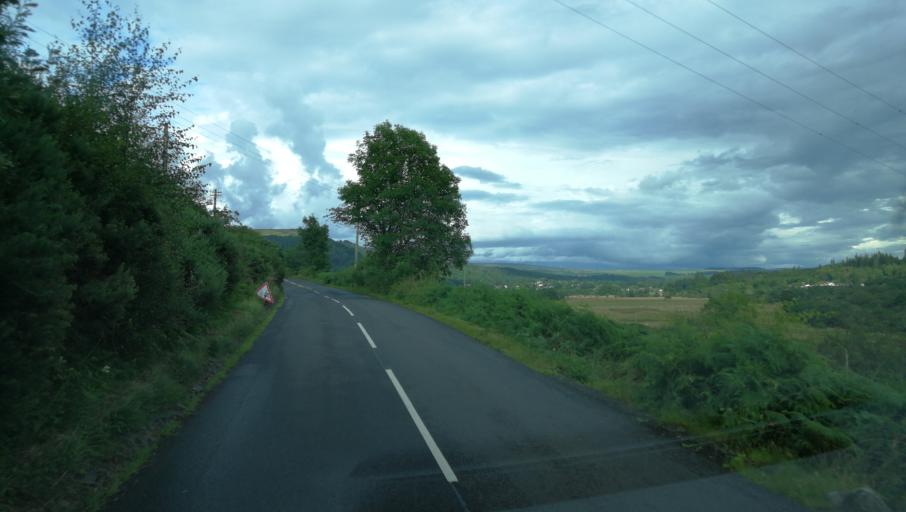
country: GB
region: Scotland
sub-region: Stirling
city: Callander
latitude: 56.2399
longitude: -4.2516
